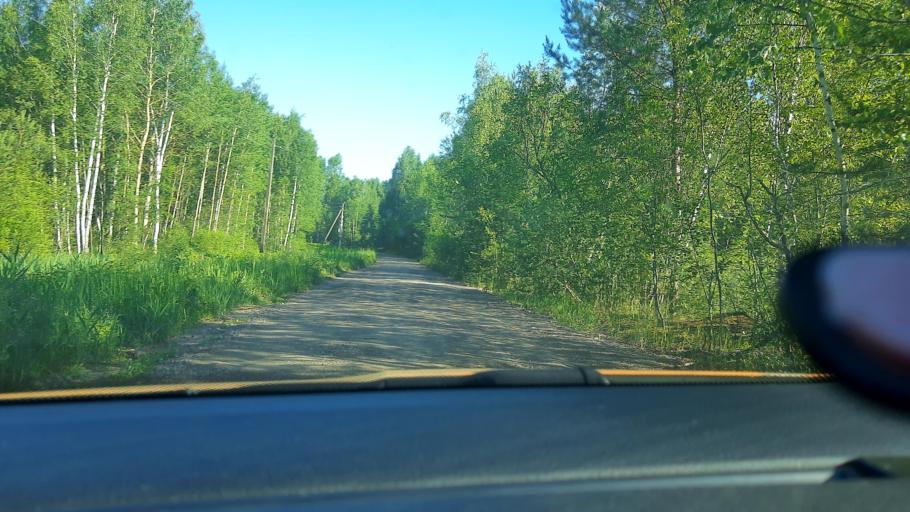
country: RU
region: Moskovskaya
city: Elektrogorsk
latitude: 55.8959
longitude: 38.7159
